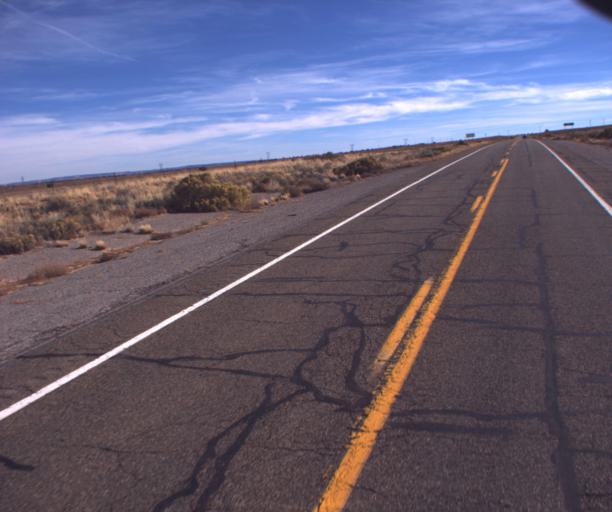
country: US
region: Arizona
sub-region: Coconino County
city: Kaibito
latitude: 36.6172
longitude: -110.9583
